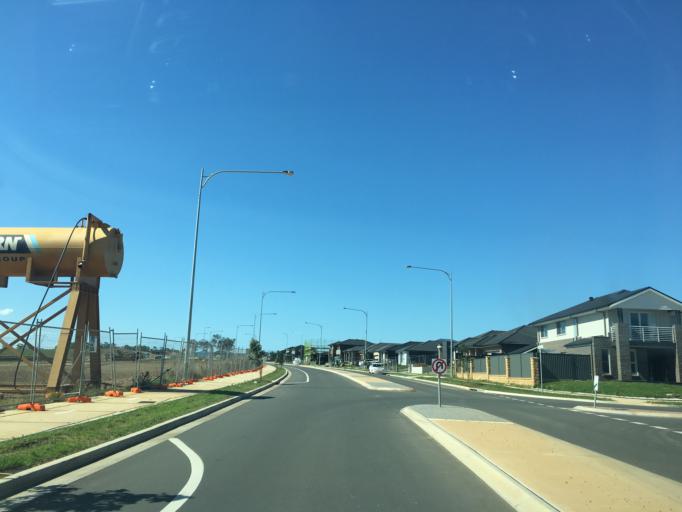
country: AU
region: New South Wales
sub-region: Campbelltown Municipality
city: Denham Court
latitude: -33.9953
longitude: 150.7942
